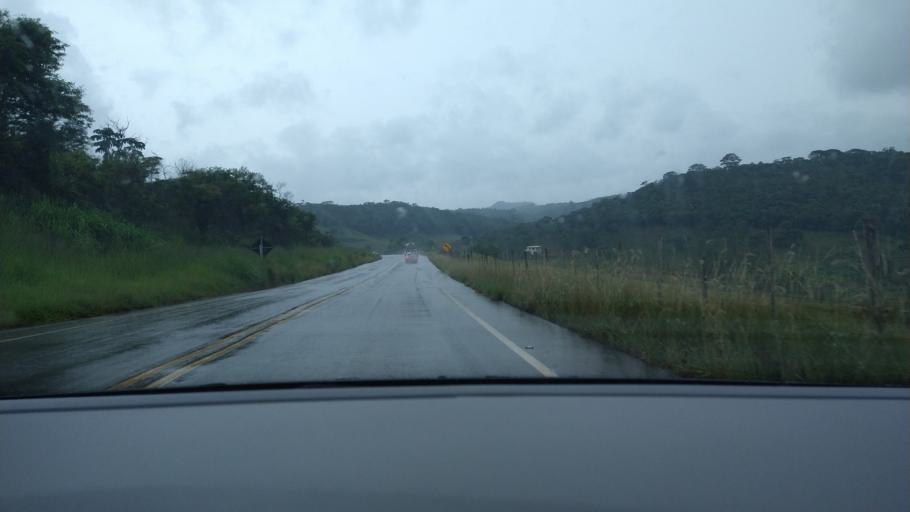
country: BR
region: Minas Gerais
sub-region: Vicosa
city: Vicosa
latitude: -20.6079
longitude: -42.8678
